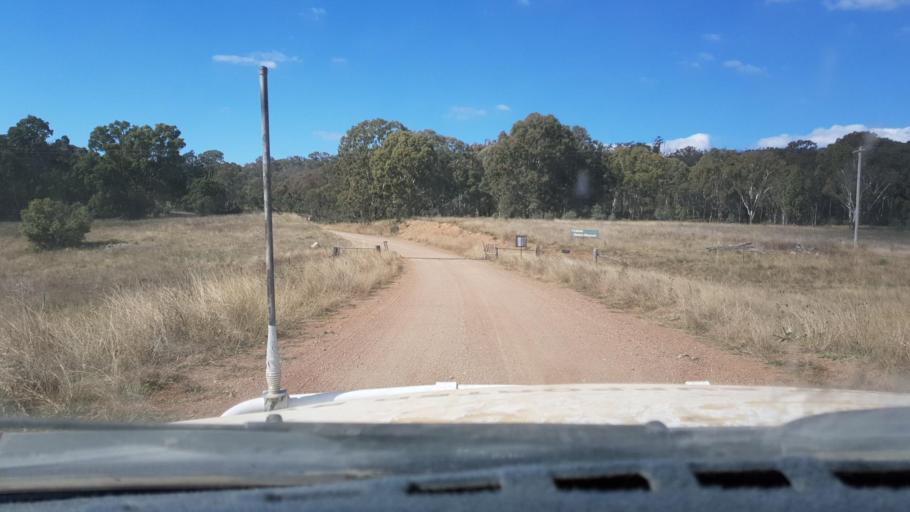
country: AU
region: New South Wales
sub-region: Tamworth Municipality
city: Manilla
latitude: -30.4445
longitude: 150.8657
